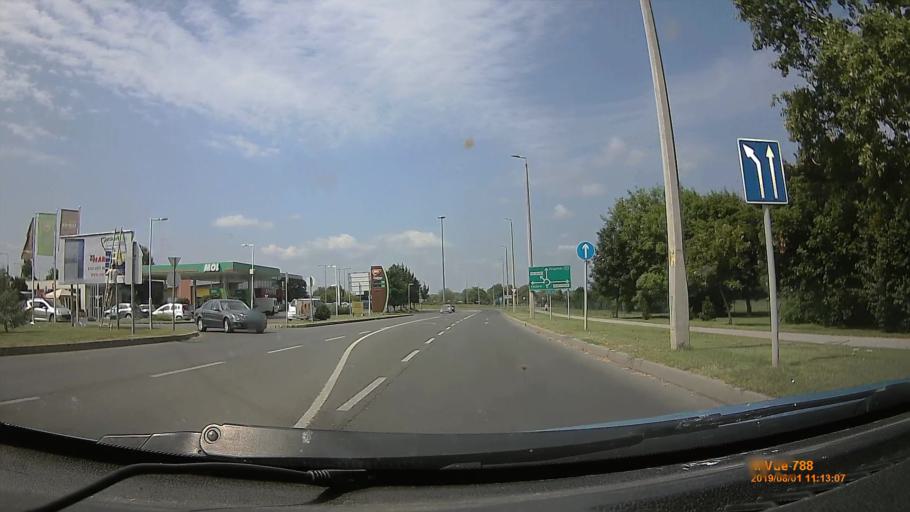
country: HU
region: Baranya
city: Pecs
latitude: 46.0422
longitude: 18.2147
